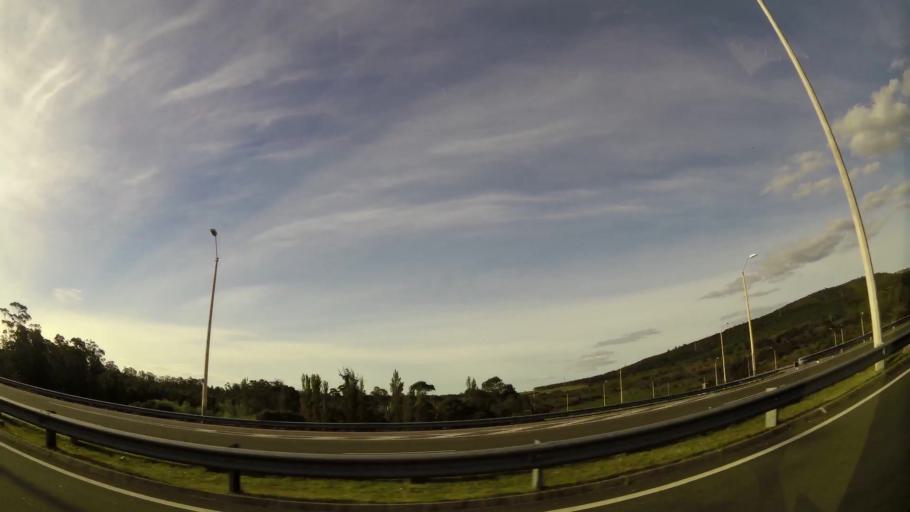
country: UY
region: Maldonado
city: Piriapolis
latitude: -34.7776
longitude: -55.3539
